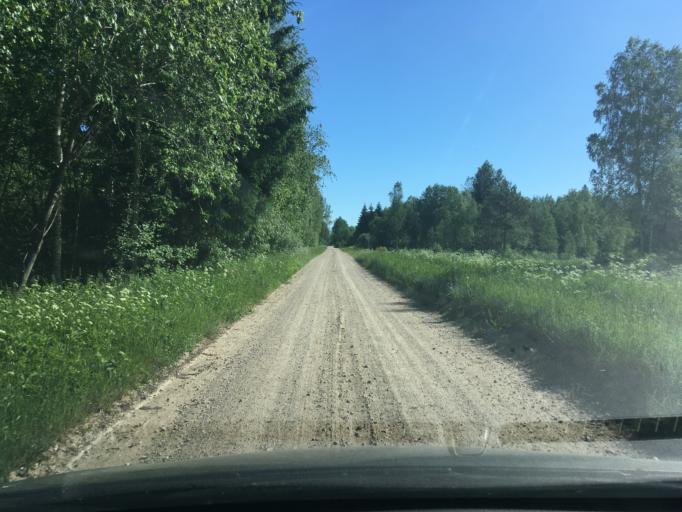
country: EE
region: Laeaene
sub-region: Lihula vald
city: Lihula
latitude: 58.6445
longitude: 23.7764
